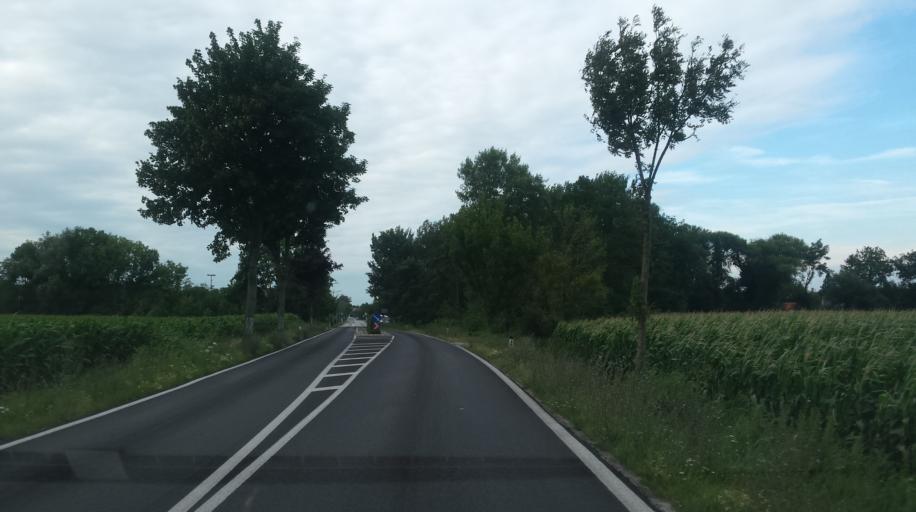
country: AT
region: Lower Austria
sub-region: Politischer Bezirk Wien-Umgebung
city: Moosbrunn
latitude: 48.0094
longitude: 16.4525
